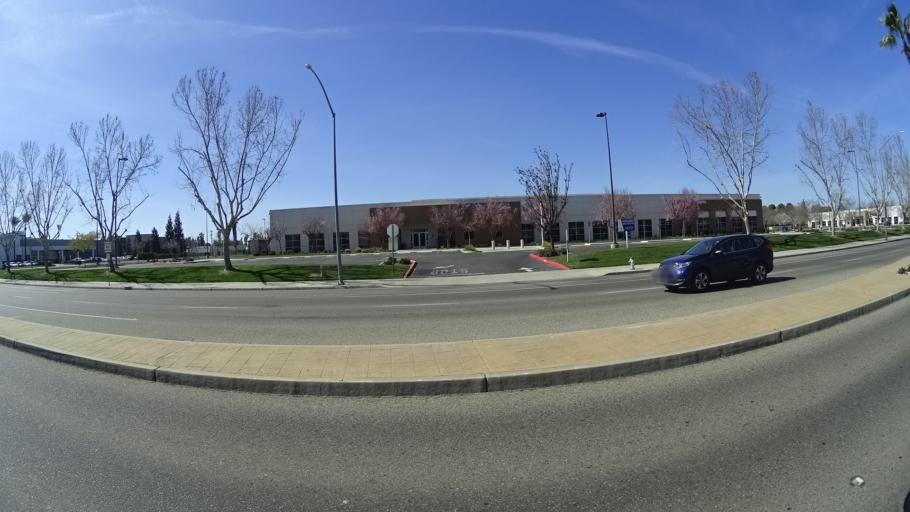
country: US
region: California
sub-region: Fresno County
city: Fresno
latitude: 36.8405
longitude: -119.8087
